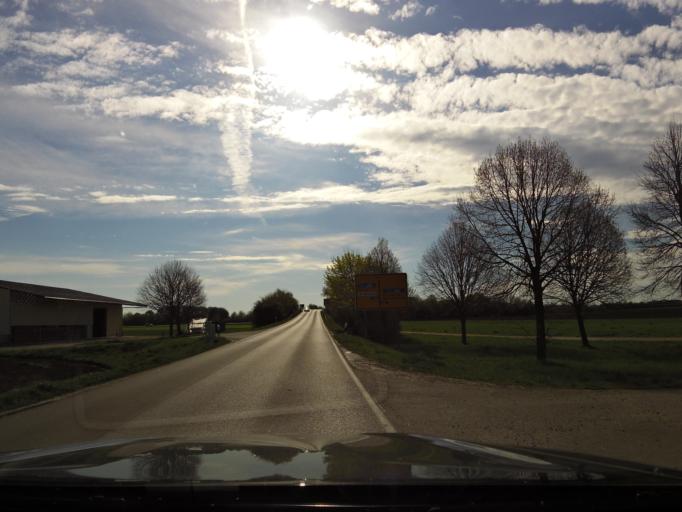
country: DE
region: Bavaria
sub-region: Upper Bavaria
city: Stammham
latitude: 48.3209
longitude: 11.8788
